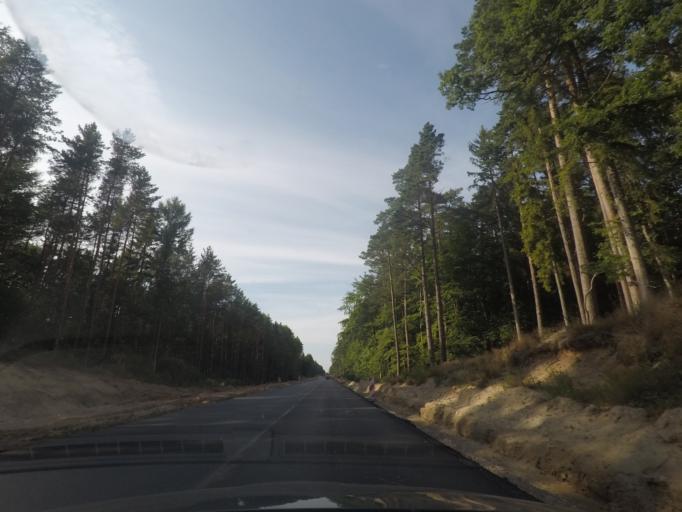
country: PL
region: Pomeranian Voivodeship
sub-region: Powiat leborski
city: Leba
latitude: 54.6987
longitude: 17.5888
